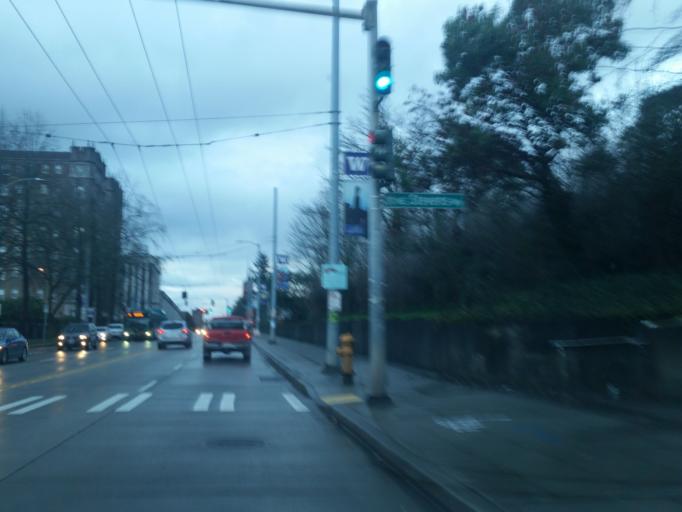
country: US
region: Washington
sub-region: King County
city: Seattle
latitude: 47.6598
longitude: -122.3119
